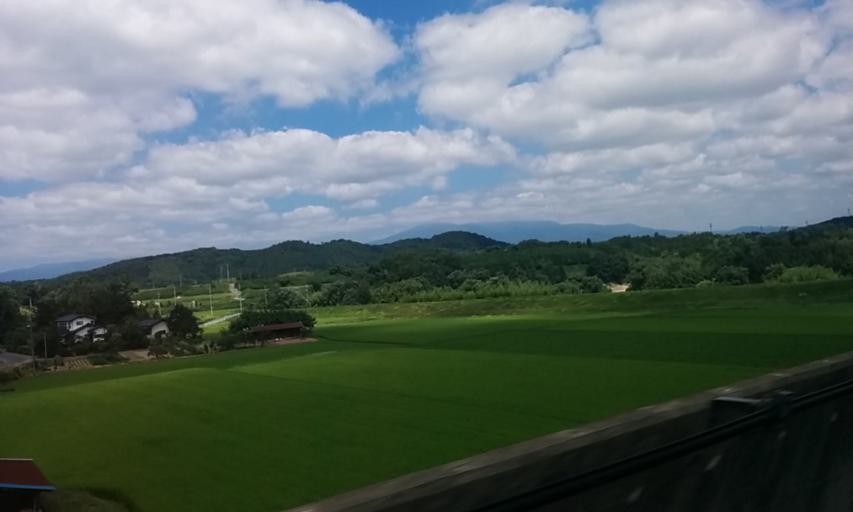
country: JP
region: Fukushima
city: Motomiya
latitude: 37.4612
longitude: 140.4102
